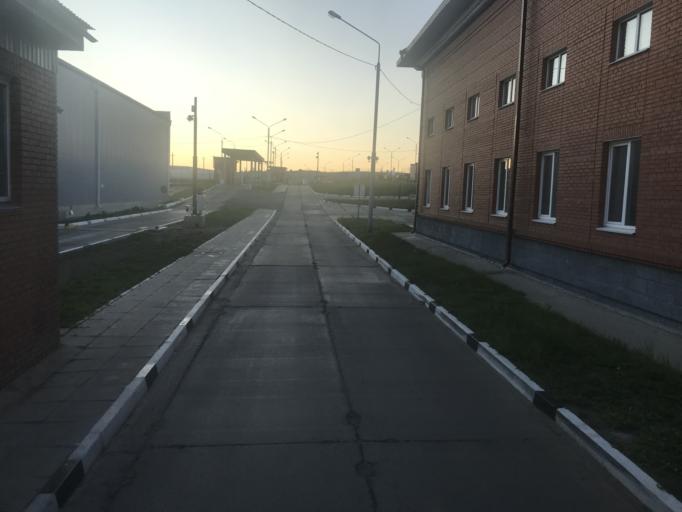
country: MN
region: Selenge
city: Altanbulag
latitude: 50.3263
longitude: 106.4862
